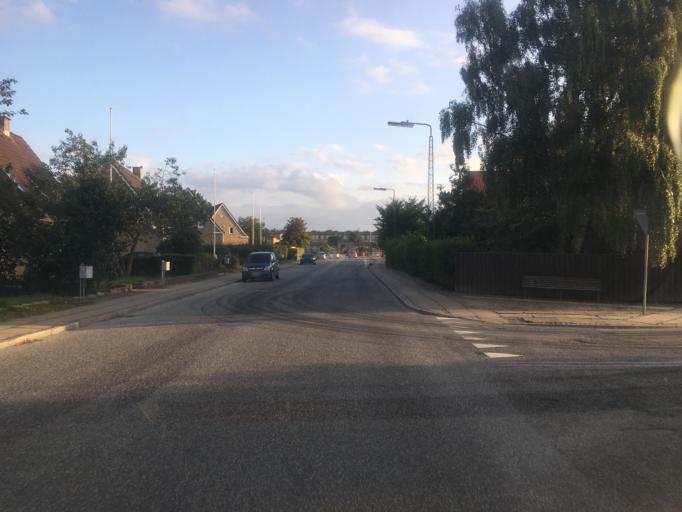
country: DK
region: South Denmark
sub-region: Tonder Kommune
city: Tonder
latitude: 54.9465
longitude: 8.8792
